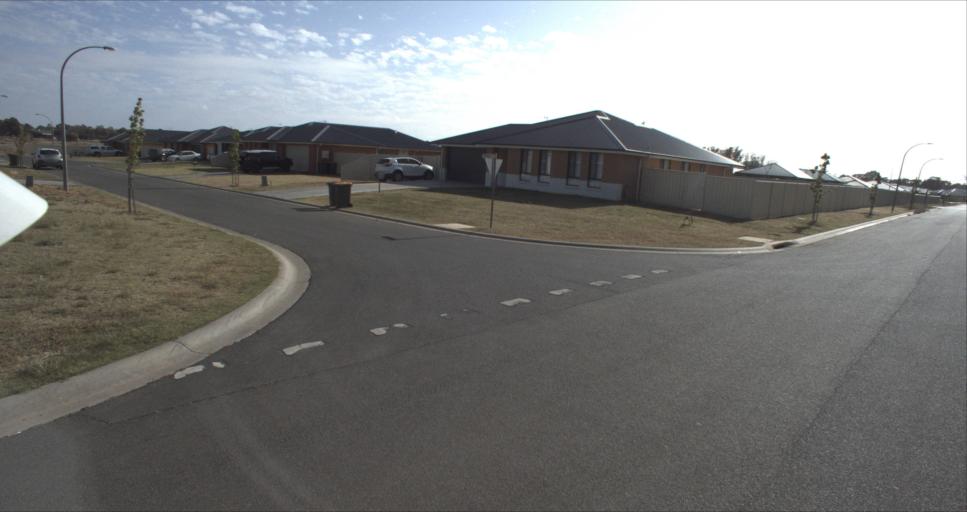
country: AU
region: New South Wales
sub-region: Leeton
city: Leeton
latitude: -34.5705
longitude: 146.3993
